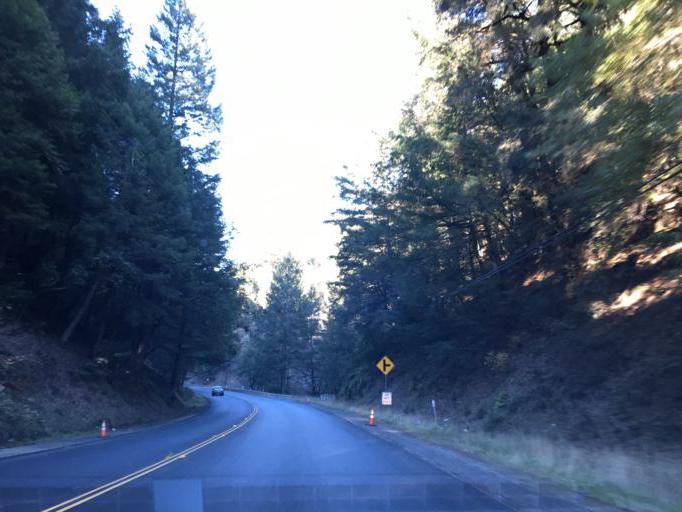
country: US
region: California
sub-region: Mendocino County
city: Laytonville
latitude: 39.7960
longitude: -123.5424
